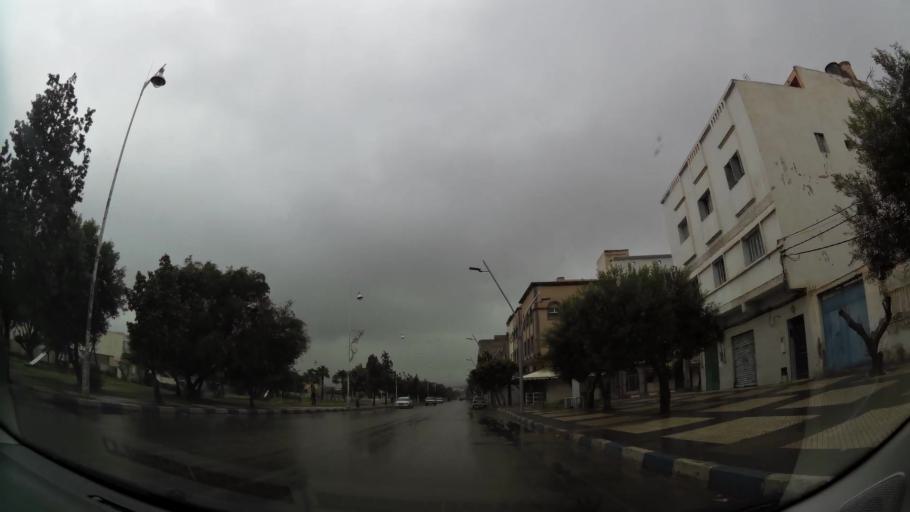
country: MA
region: Oriental
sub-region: Nador
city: Nador
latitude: 35.1656
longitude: -2.9539
